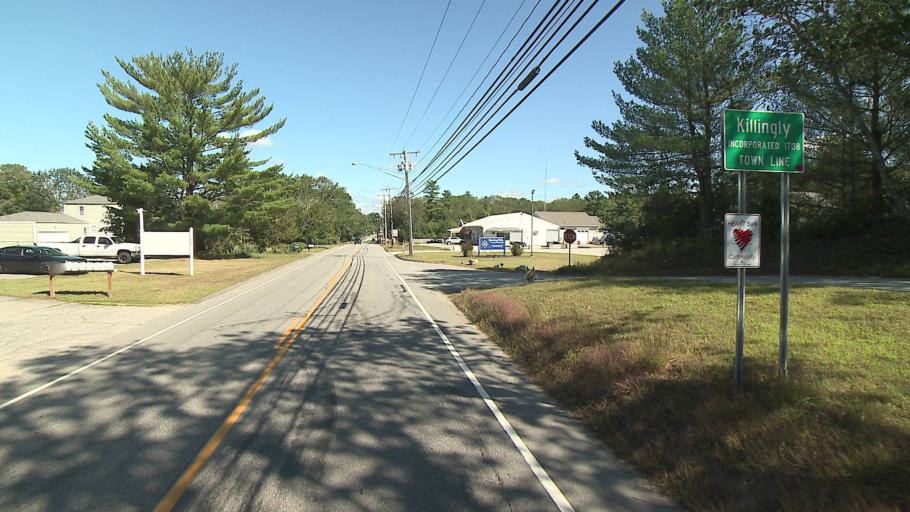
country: US
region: Connecticut
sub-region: Windham County
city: Wauregan
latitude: 41.7615
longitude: -71.9001
